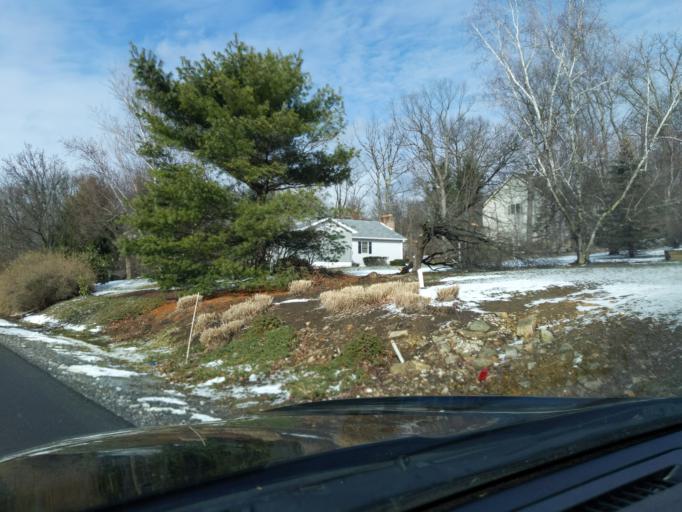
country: US
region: Pennsylvania
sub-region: Blair County
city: Lakemont
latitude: 40.4692
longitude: -78.3743
